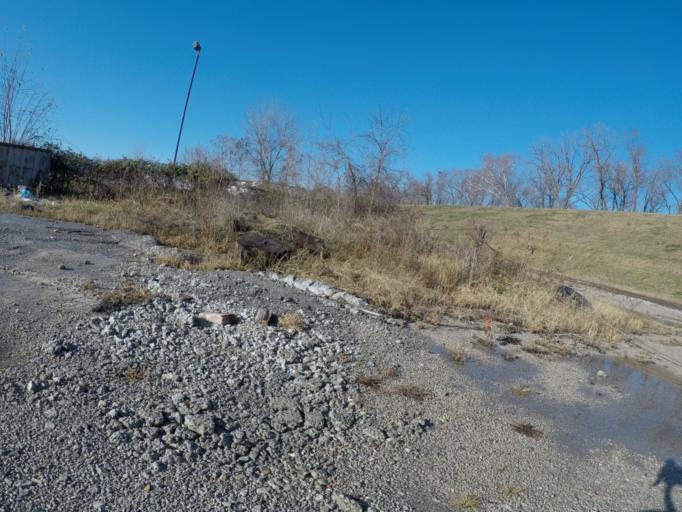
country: US
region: West Virginia
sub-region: Cabell County
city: Huntington
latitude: 38.4147
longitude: -82.4810
